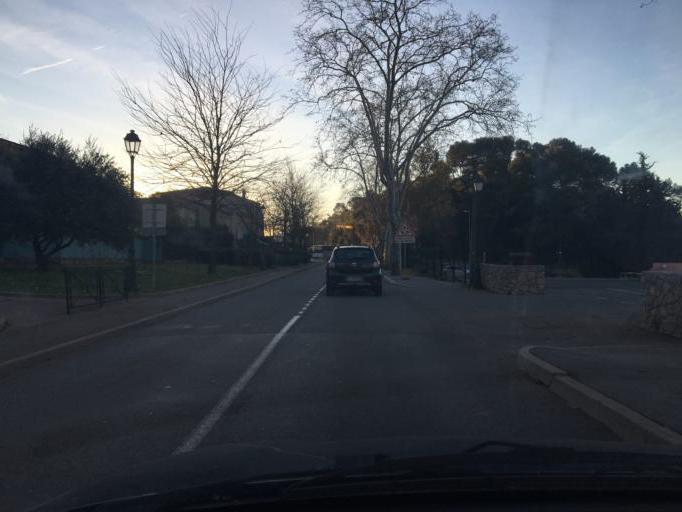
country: FR
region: Provence-Alpes-Cote d'Azur
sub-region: Departement du Var
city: Taradeau
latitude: 43.4529
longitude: 6.4287
